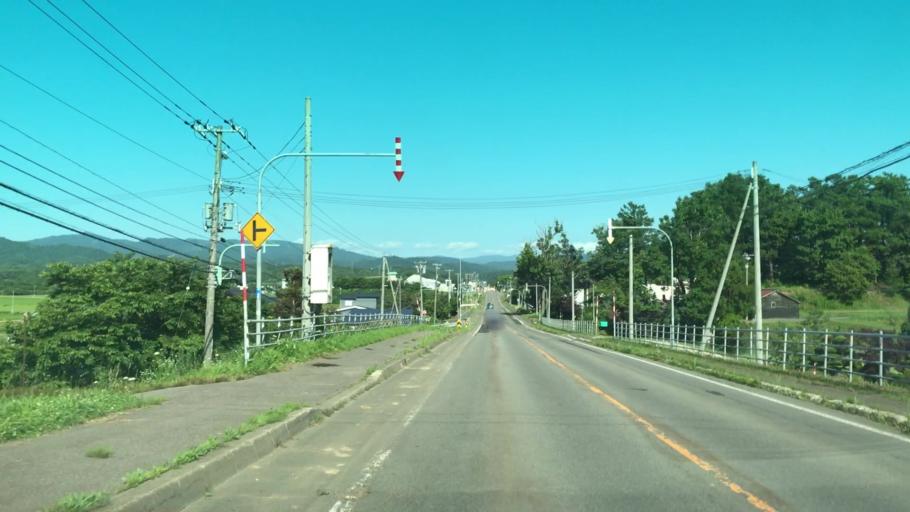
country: JP
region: Hokkaido
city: Iwanai
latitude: 42.9802
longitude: 140.5987
